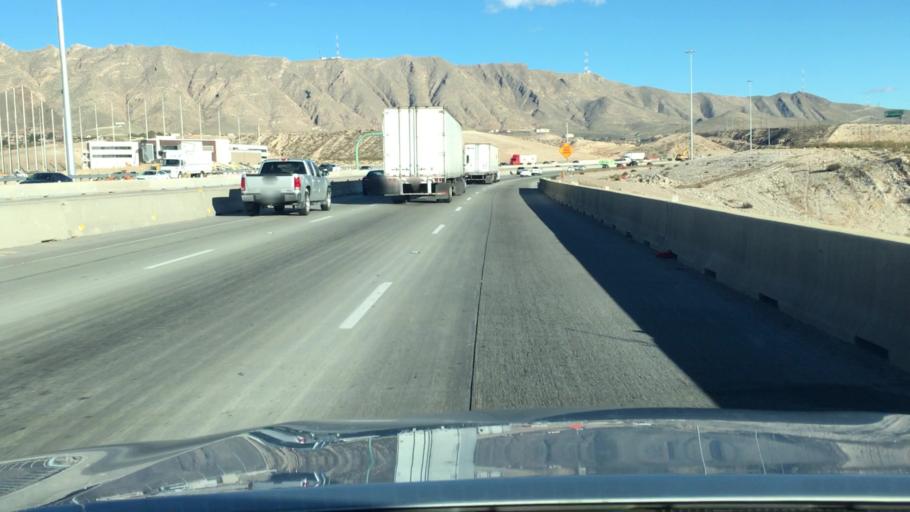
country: US
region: New Mexico
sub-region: Dona Ana County
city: Sunland Park
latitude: 31.8092
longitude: -106.5298
